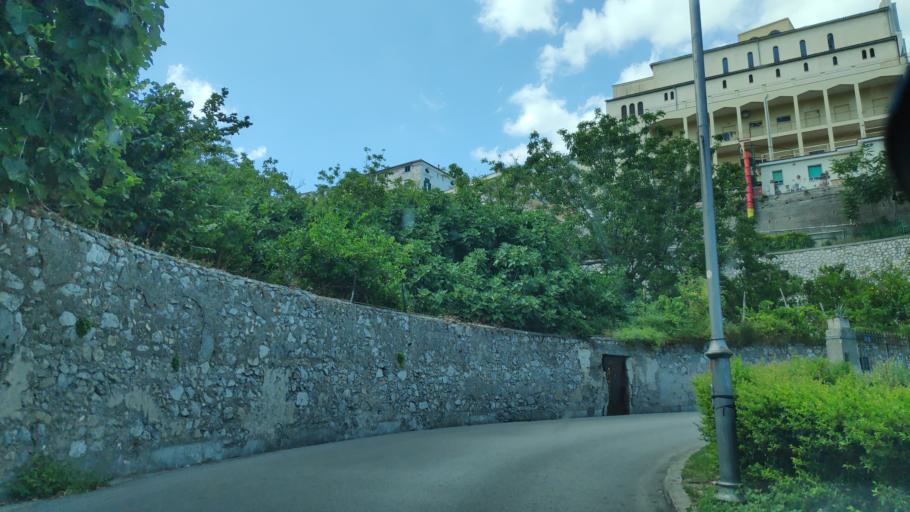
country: IT
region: Campania
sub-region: Provincia di Salerno
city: Vietri sul Mare
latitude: 40.6700
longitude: 14.7307
